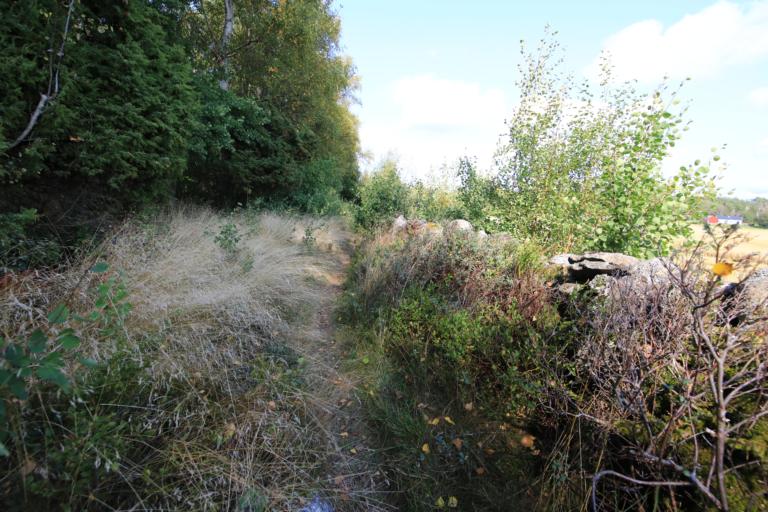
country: SE
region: Halland
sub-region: Varbergs Kommun
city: Varberg
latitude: 57.1726
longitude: 12.2132
